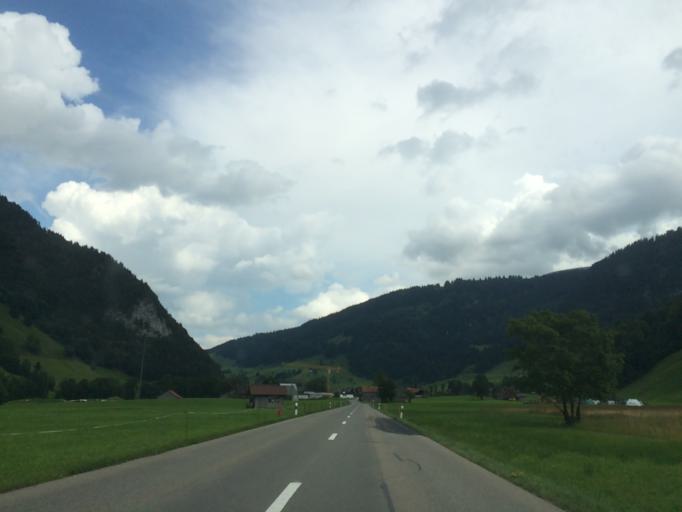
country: CH
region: Saint Gallen
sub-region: Wahlkreis Sarganserland
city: Quarten
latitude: 47.1877
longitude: 9.2411
